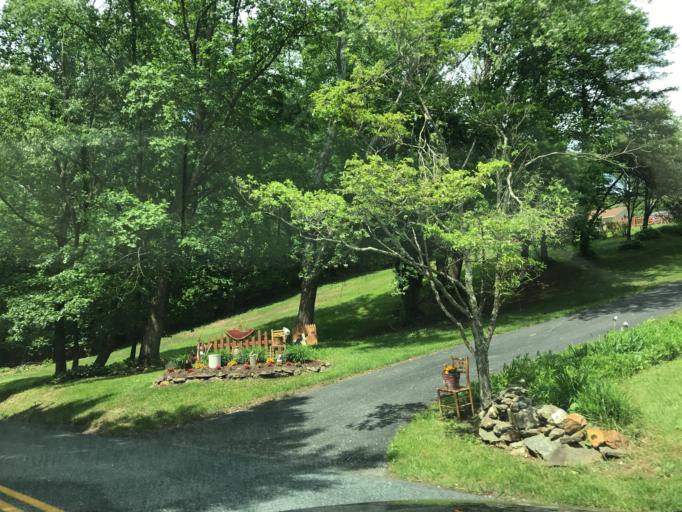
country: US
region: Maryland
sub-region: Harford County
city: Bel Air North
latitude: 39.6002
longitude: -76.3449
